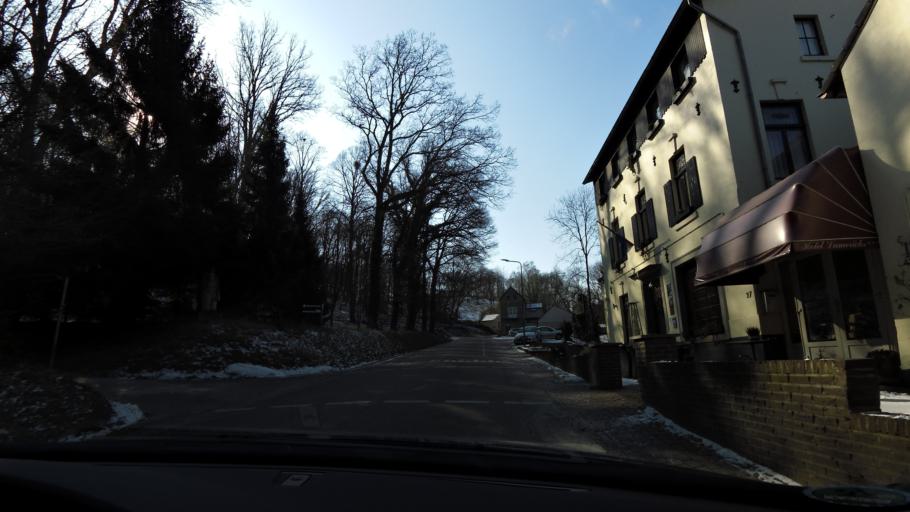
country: NL
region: Limburg
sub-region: Valkenburg aan de Geul
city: Berg
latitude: 50.8671
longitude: 5.7831
